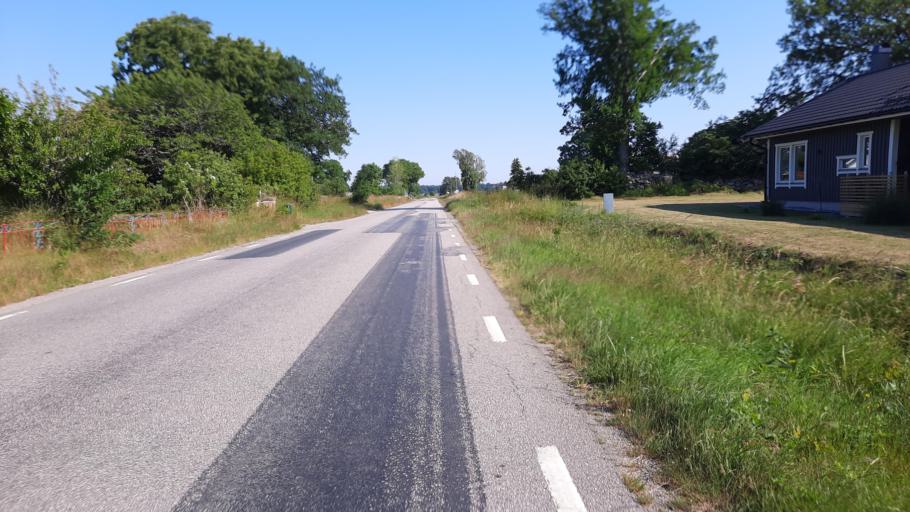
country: SE
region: Blekinge
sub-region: Karlskrona Kommun
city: Sturko
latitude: 56.1077
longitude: 15.6856
